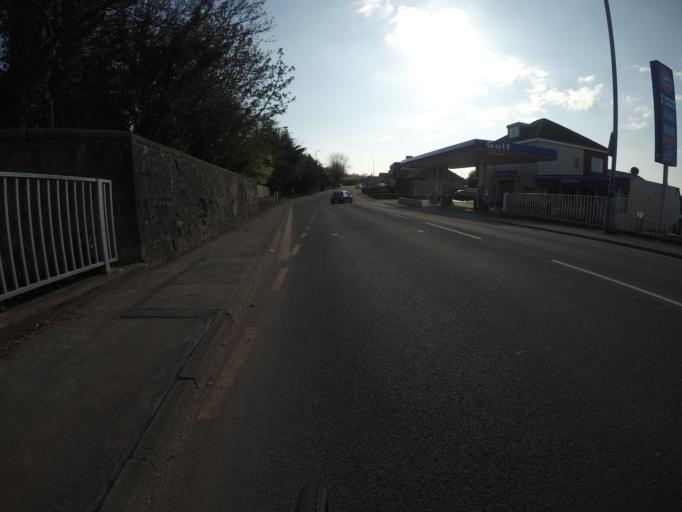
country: GB
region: Scotland
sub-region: North Ayrshire
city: Kilwinning
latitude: 55.6551
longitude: -4.7108
